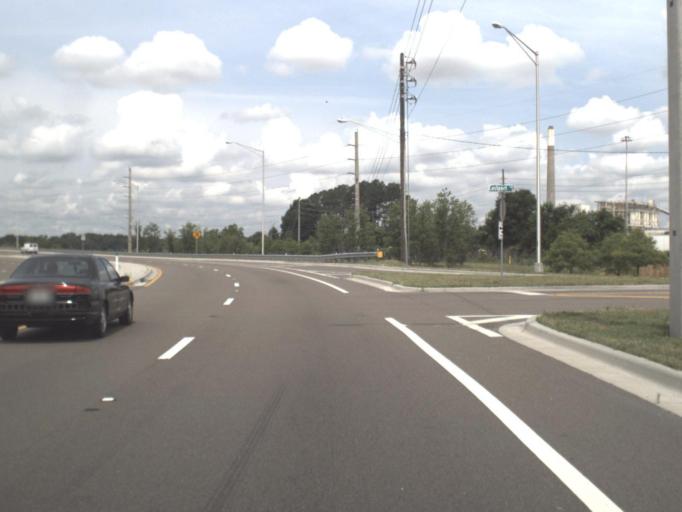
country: US
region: Florida
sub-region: Duval County
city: Jacksonville
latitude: 30.4178
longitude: -81.5982
